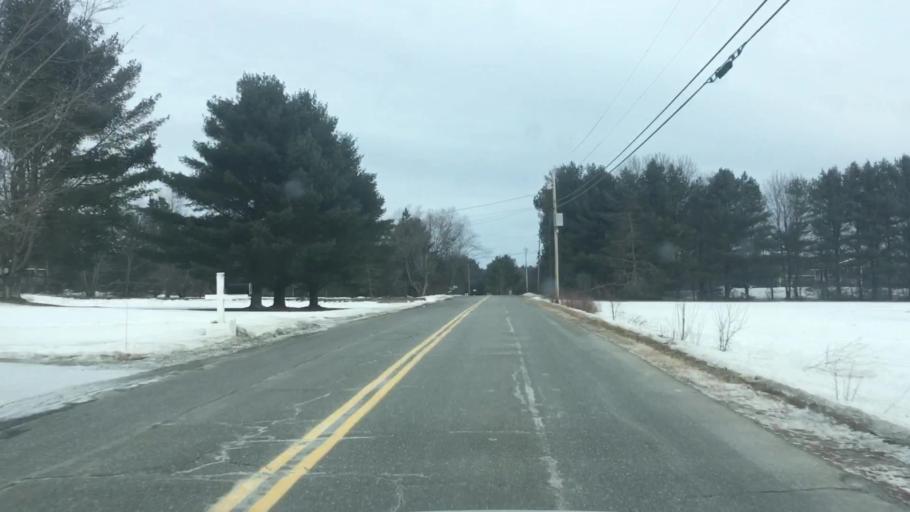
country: US
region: Maine
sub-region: Kennebec County
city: Chelsea
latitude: 44.2997
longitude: -69.6970
